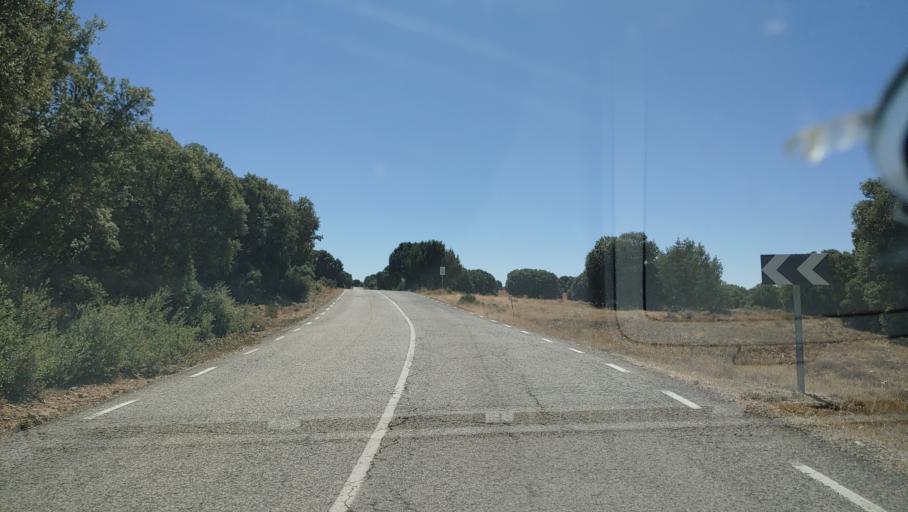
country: ES
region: Castille-La Mancha
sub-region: Provincia de Albacete
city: Ossa de Montiel
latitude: 38.8923
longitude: -2.7695
